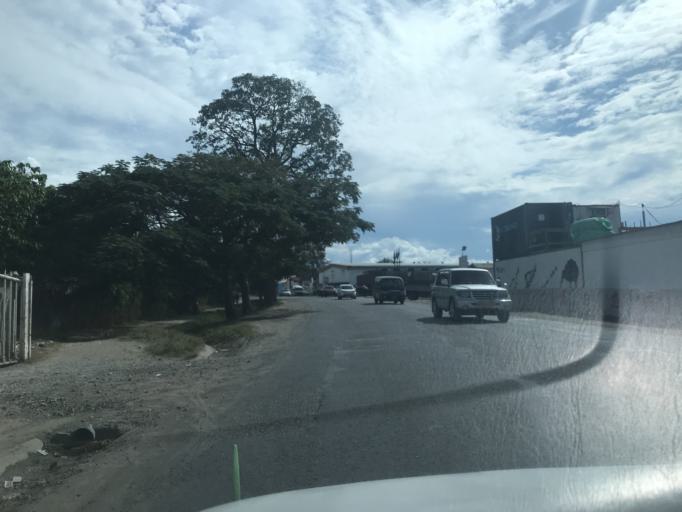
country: SB
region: Guadalcanal
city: Honiara
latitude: -9.4298
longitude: 159.9487
